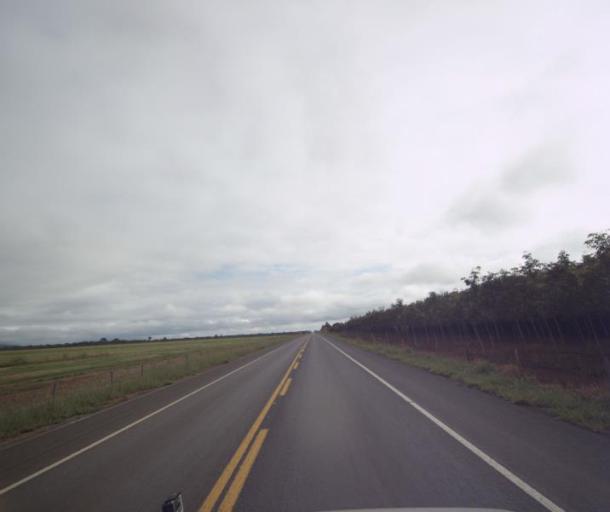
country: BR
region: Goias
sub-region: Padre Bernardo
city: Padre Bernardo
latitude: -15.3767
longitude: -48.6454
